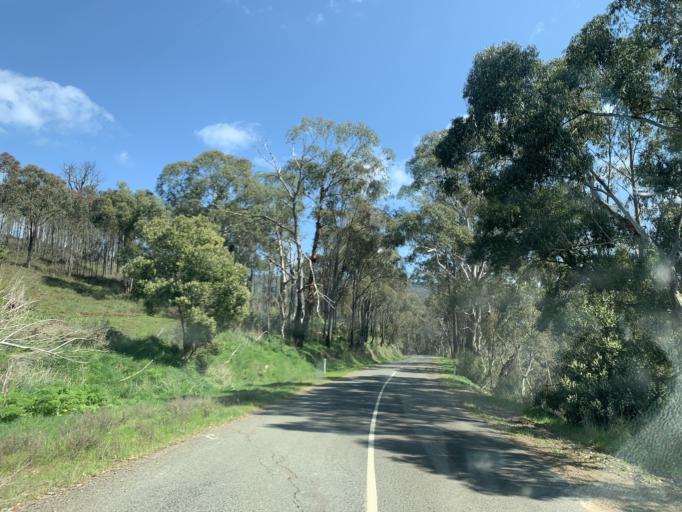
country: AU
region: Victoria
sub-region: Mansfield
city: Mansfield
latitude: -36.8274
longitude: 146.1325
